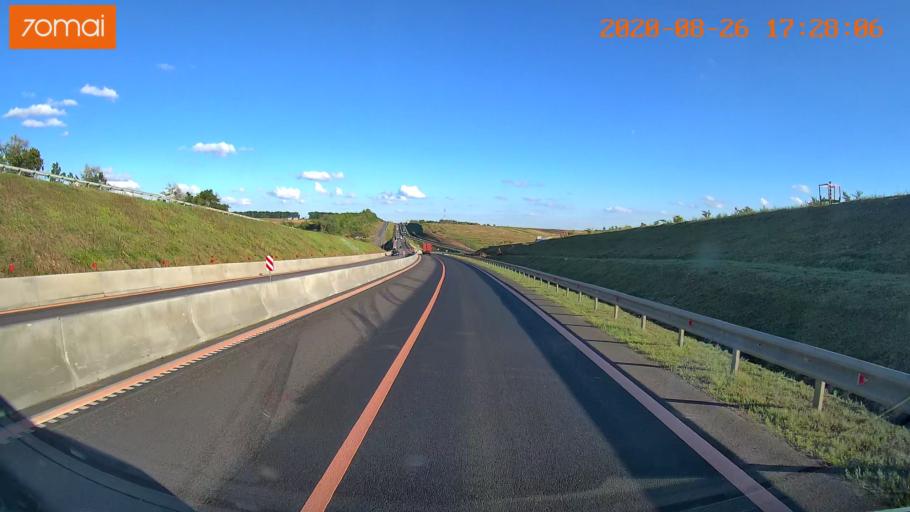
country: RU
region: Tula
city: Kazachka
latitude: 53.4659
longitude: 38.1298
